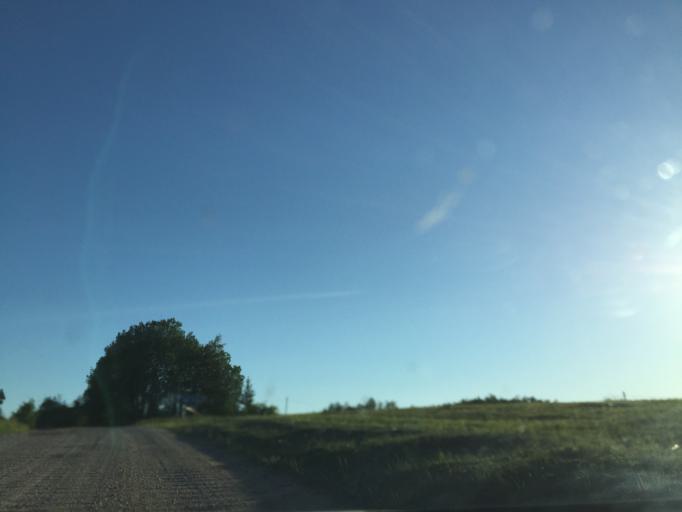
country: LV
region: Broceni
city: Broceni
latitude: 56.7779
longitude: 22.5409
